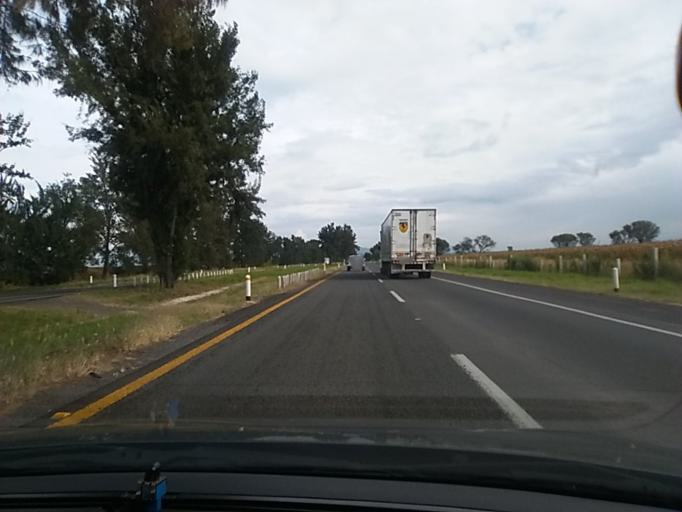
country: MX
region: Michoacan
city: Vistahermosa de Negrete
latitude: 20.3022
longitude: -102.4850
